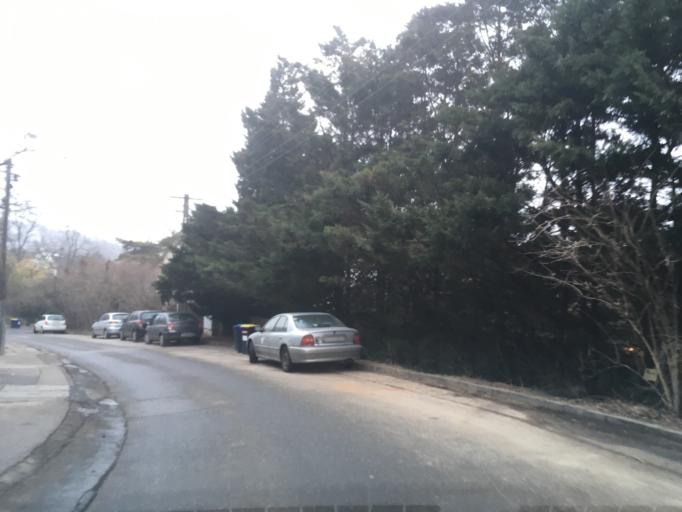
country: HU
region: Budapest
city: Budapest XII. keruelet
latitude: 47.5288
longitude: 18.9903
